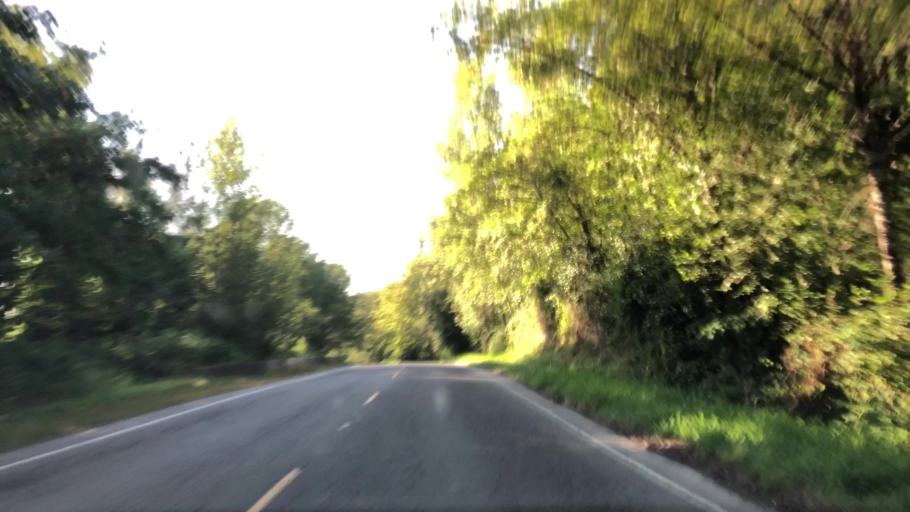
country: US
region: Washington
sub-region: King County
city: Woodinville
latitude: 47.7672
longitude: -122.1755
